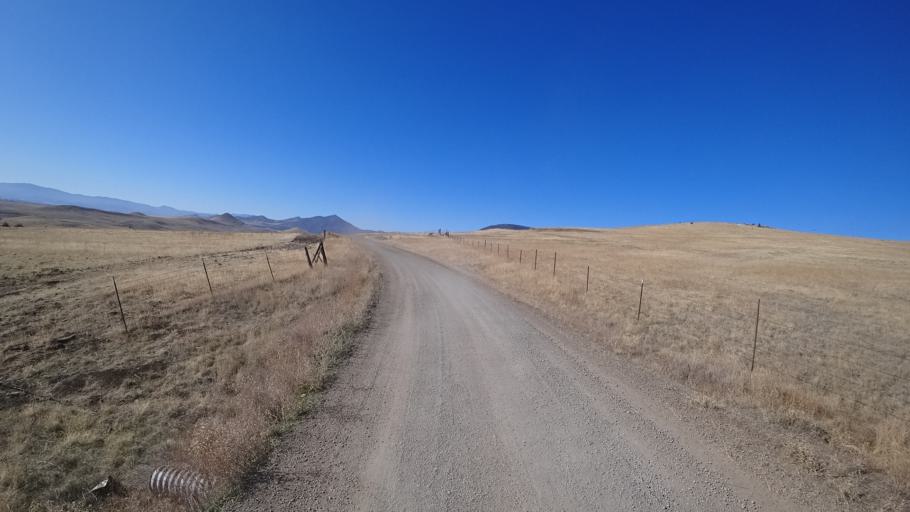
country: US
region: California
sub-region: Siskiyou County
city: Montague
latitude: 41.8445
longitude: -122.4235
